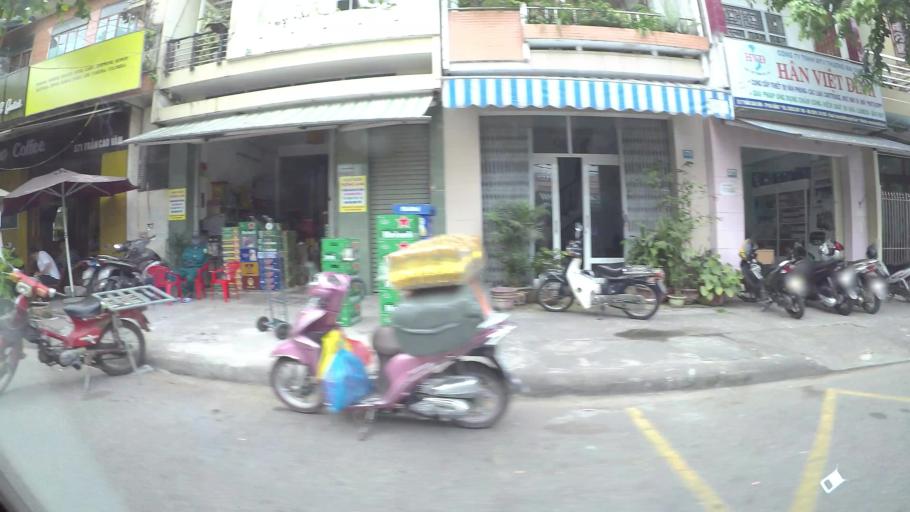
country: VN
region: Da Nang
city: Thanh Khe
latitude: 16.0714
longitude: 108.1879
